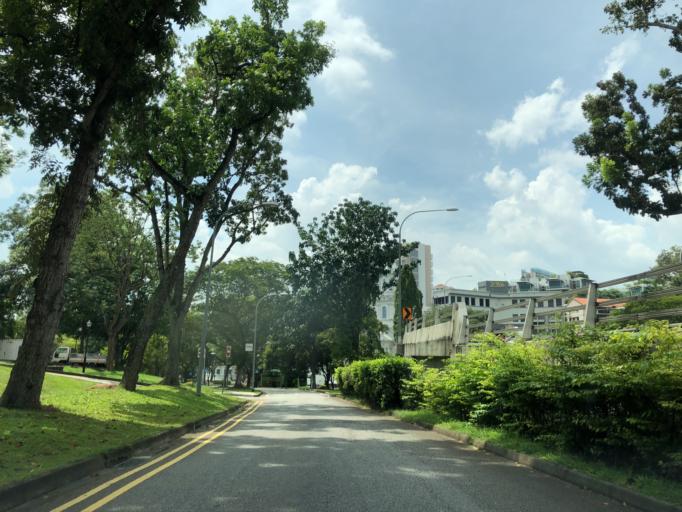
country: SG
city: Singapore
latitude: 1.2969
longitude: 103.8450
